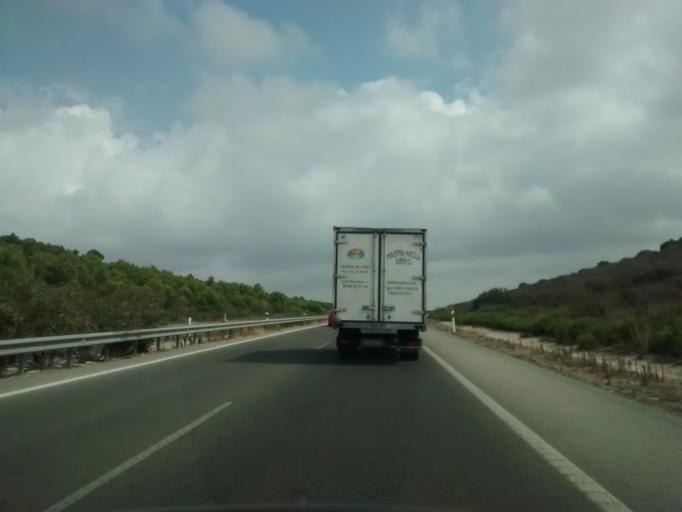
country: ES
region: Andalusia
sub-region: Provincia de Cadiz
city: Conil de la Frontera
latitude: 36.3233
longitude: -6.0561
